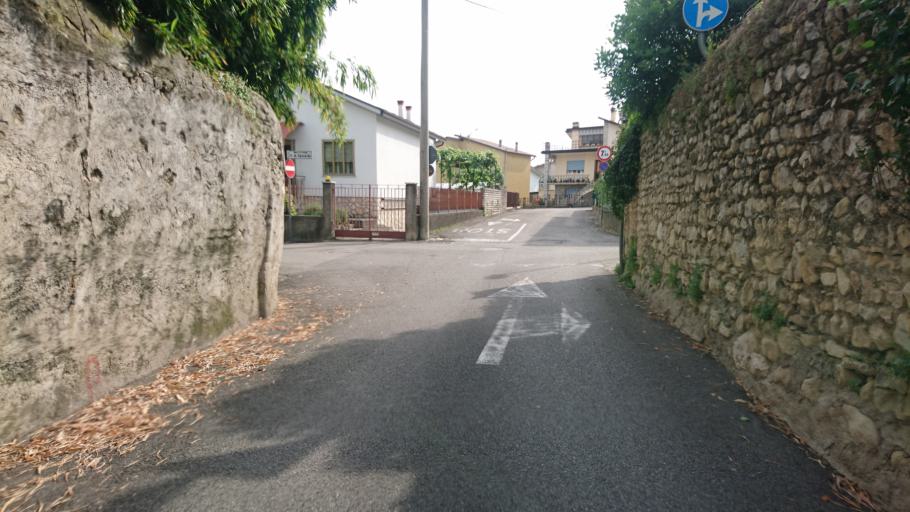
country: IT
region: Veneto
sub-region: Provincia di Treviso
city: Vittorio Veneto
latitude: 45.9710
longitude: 12.2928
